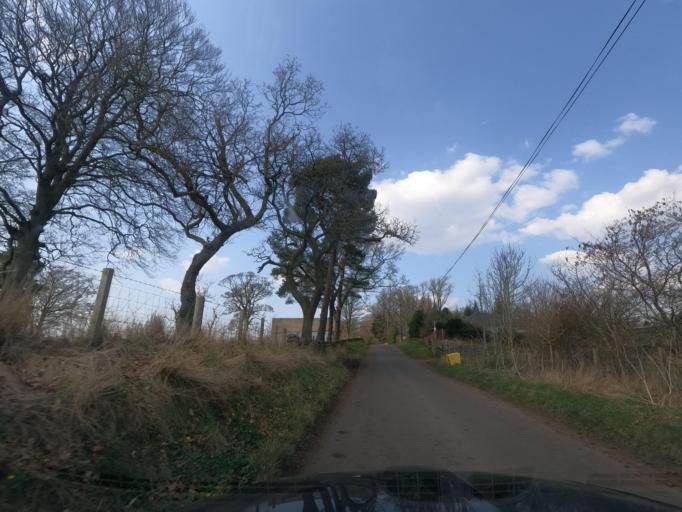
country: GB
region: Scotland
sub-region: South Lanarkshire
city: Carnwath
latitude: 55.7434
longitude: -3.6297
